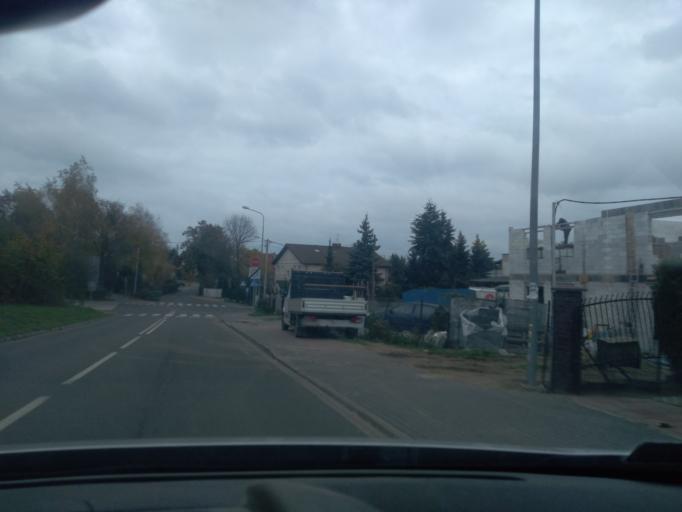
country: PL
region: Greater Poland Voivodeship
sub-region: Powiat poznanski
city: Suchy Las
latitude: 52.4772
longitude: 16.8789
